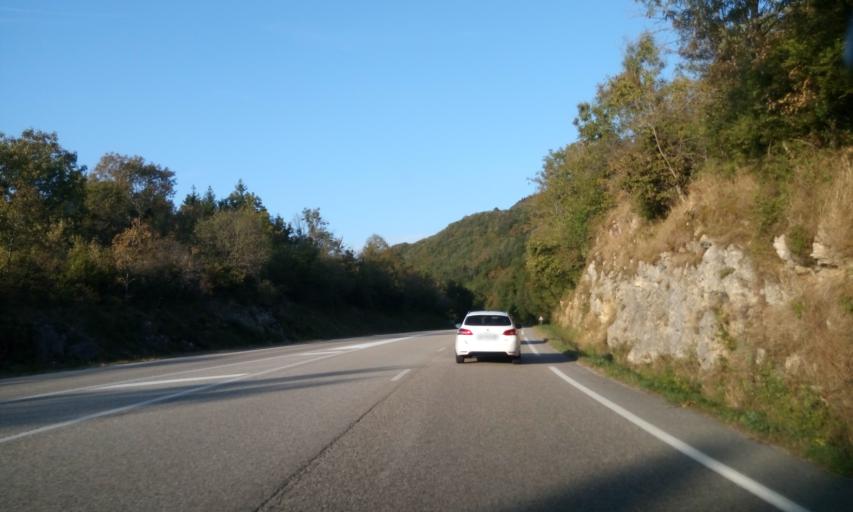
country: FR
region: Rhone-Alpes
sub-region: Departement de l'Ain
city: Poncin
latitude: 46.0977
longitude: 5.4843
